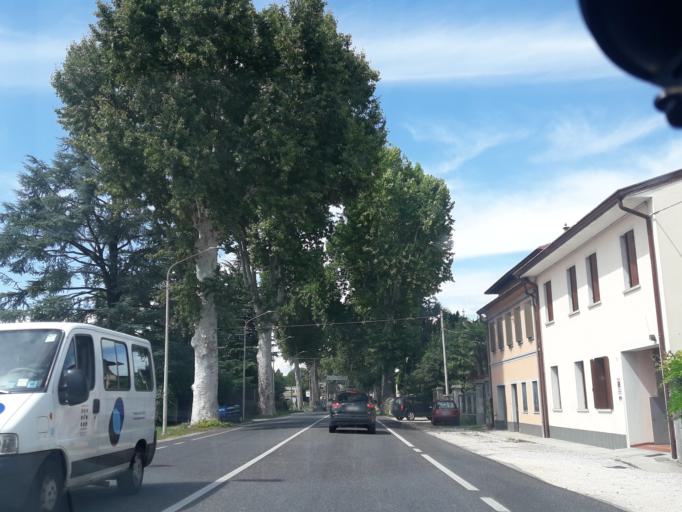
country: IT
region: Friuli Venezia Giulia
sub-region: Provincia di Udine
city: Udine
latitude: 46.0492
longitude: 13.2488
